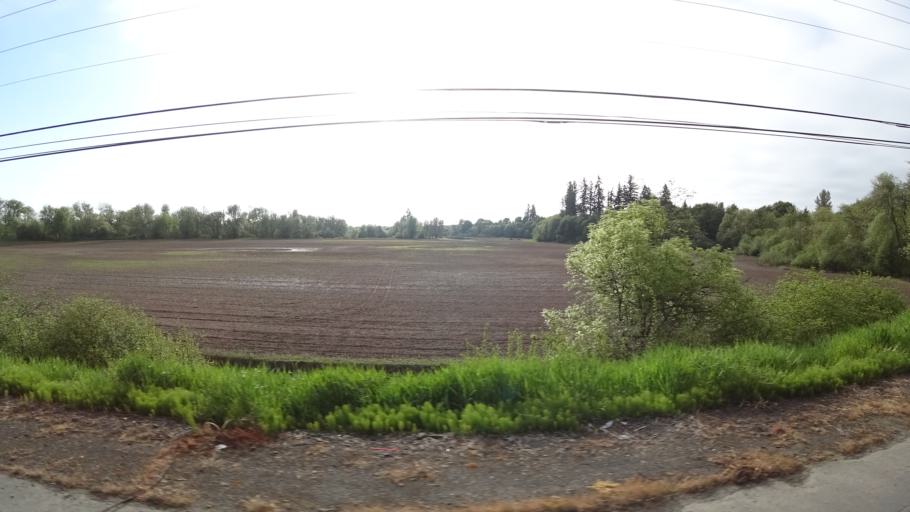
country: US
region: Oregon
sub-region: Washington County
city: Hillsboro
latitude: 45.4974
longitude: -122.9922
